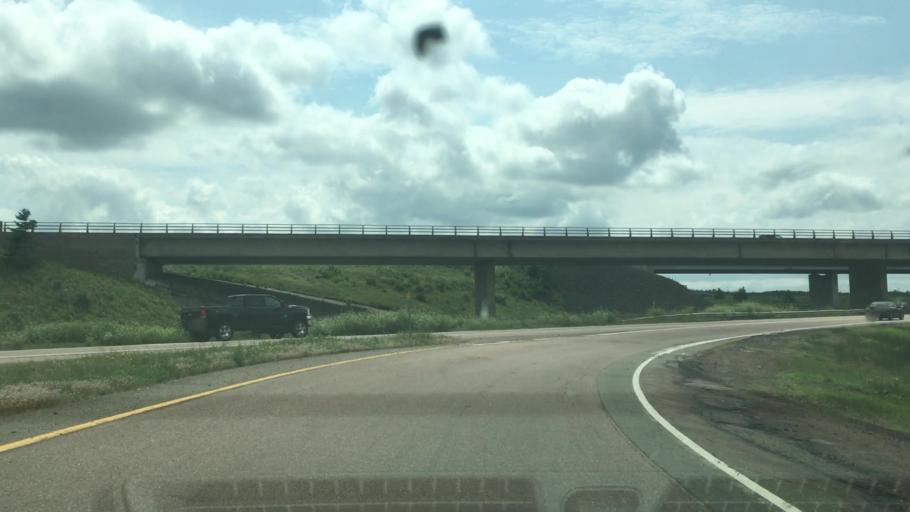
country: CA
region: New Brunswick
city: Dieppe
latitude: 46.1291
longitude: -64.6800
